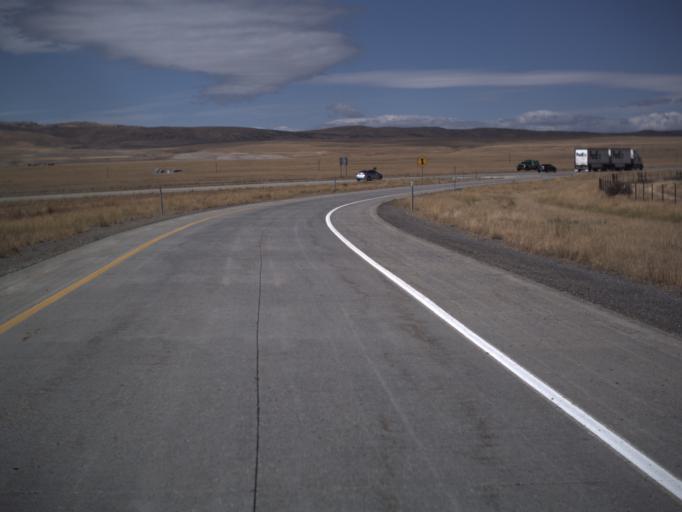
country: US
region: Utah
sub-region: Box Elder County
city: Garland
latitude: 41.8429
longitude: -112.4374
